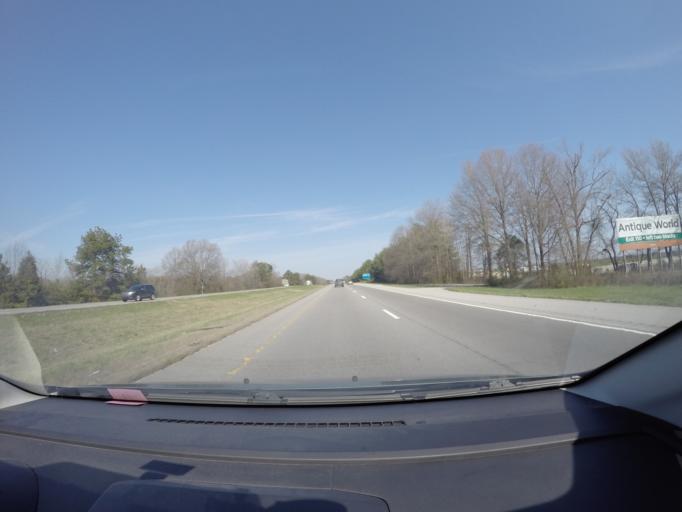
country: US
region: Tennessee
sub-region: Coffee County
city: Manchester
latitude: 35.4720
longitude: -86.0593
